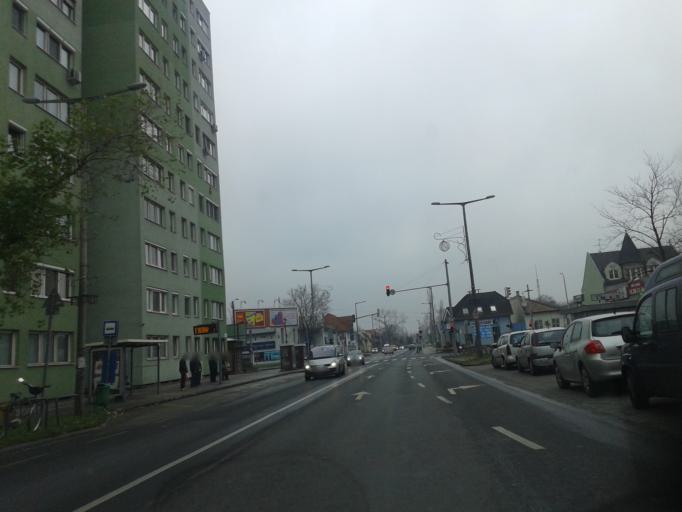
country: HU
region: Budapest
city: Budapest XXI. keruelet
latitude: 47.4344
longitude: 19.0708
